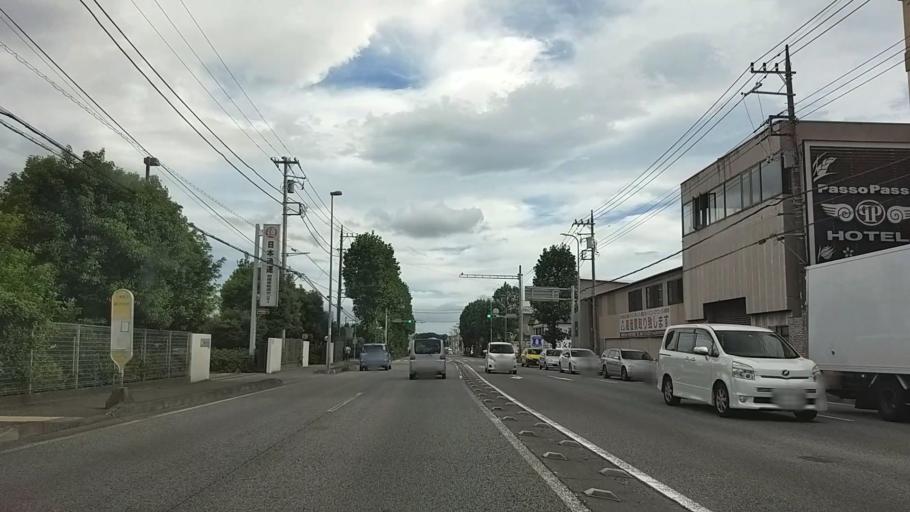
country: JP
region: Tokyo
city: Hachioji
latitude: 35.5758
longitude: 139.3486
